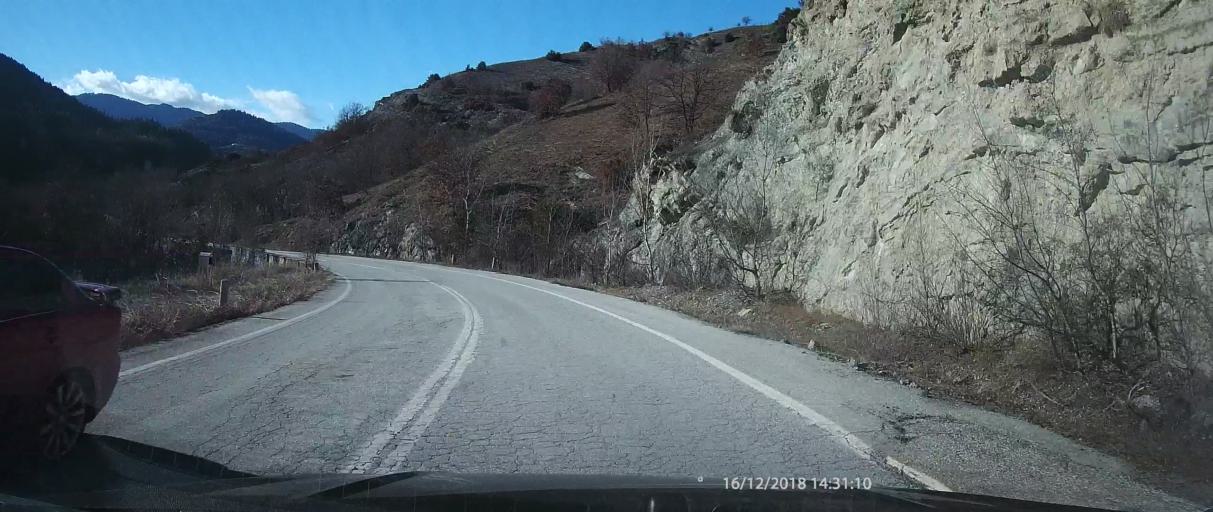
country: GR
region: West Macedonia
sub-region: Nomos Kozanis
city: Tsotili
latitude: 40.1941
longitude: 21.1845
